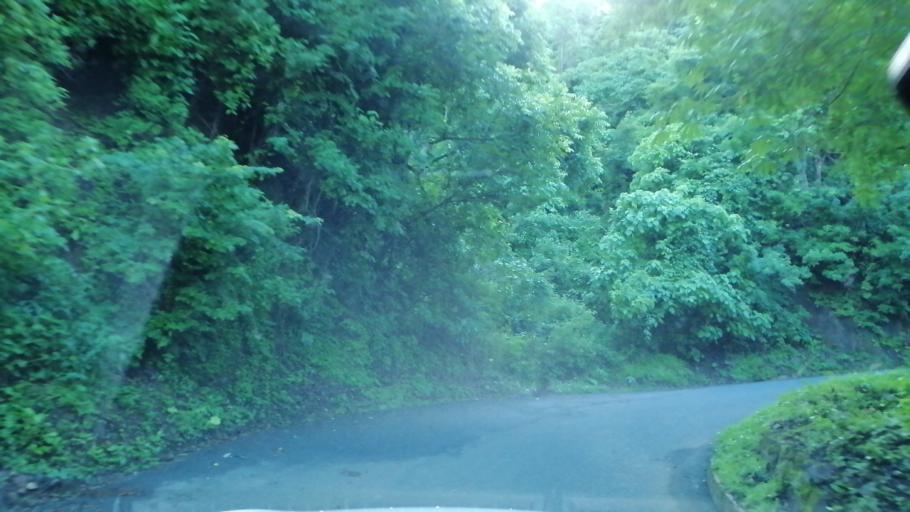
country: SV
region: Morazan
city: Cacaopera
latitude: 13.7830
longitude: -88.0351
